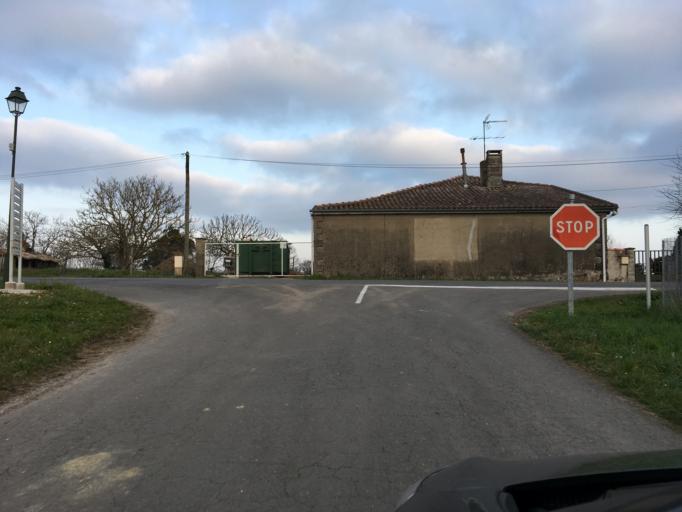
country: FR
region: Aquitaine
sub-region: Departement de la Gironde
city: Saint-Ciers-sur-Gironde
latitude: 45.3124
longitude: -0.5966
